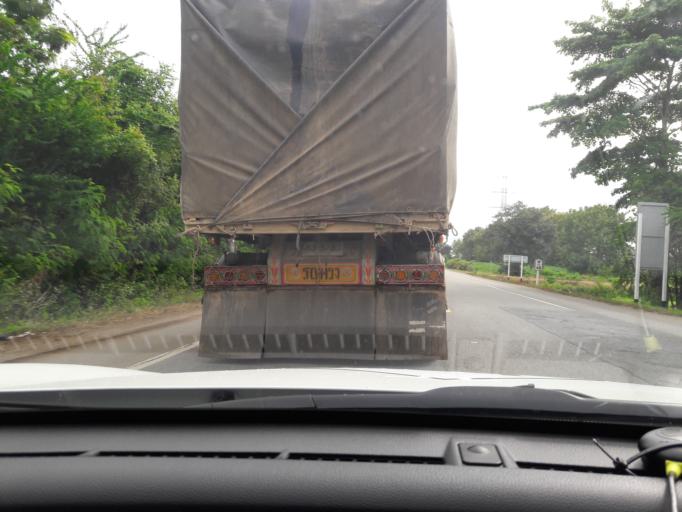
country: TH
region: Nakhon Sawan
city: Tak Fa
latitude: 15.4150
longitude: 100.5149
